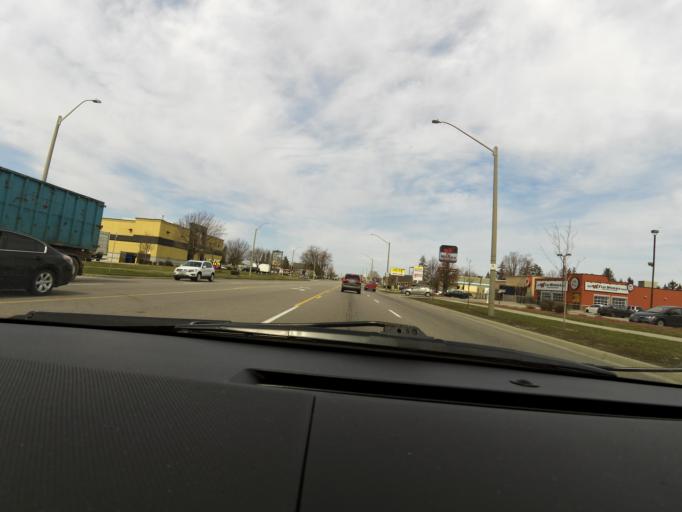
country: CA
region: Ontario
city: Hamilton
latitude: 43.2086
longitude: -79.8903
